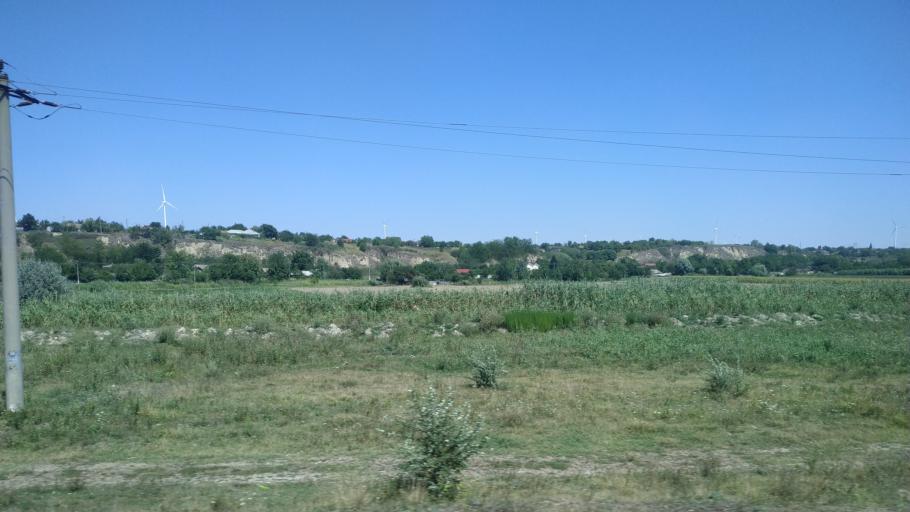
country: RO
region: Constanta
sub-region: Comuna Saligny
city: Saligny
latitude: 44.2748
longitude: 28.0928
